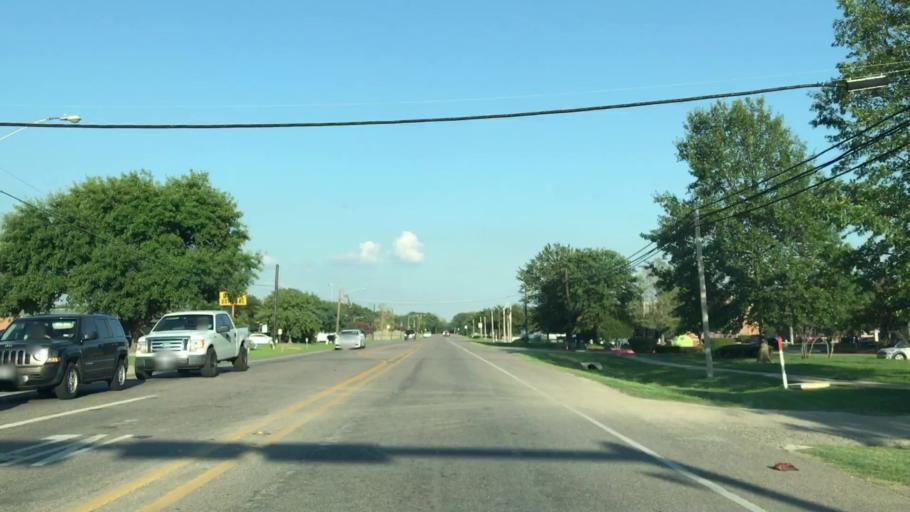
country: US
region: Texas
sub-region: Denton County
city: Denton
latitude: 33.2157
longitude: -97.1116
